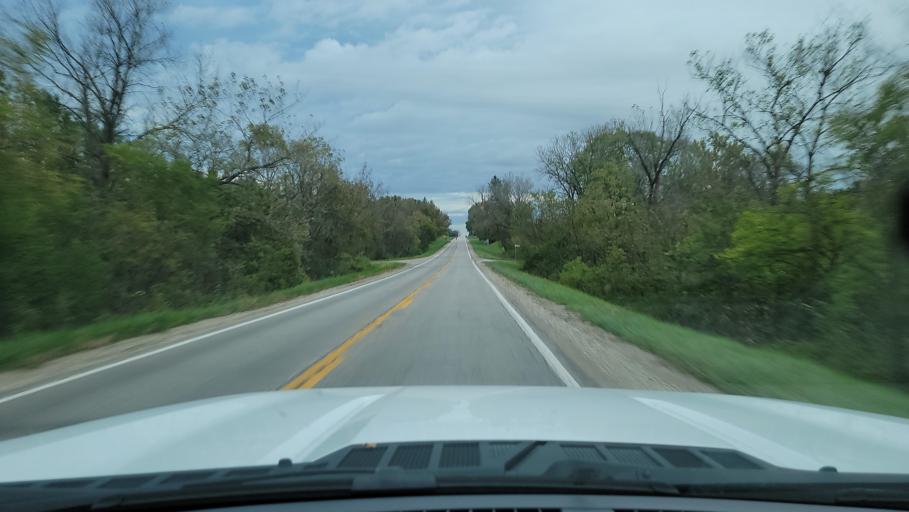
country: US
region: Illinois
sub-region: Schuyler County
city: Rushville
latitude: 40.0435
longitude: -90.6152
